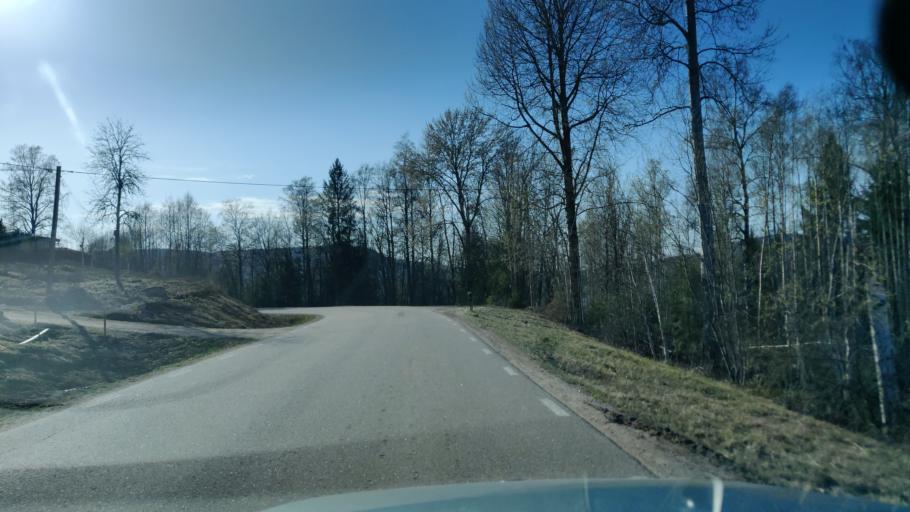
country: SE
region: Vaermland
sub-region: Munkfors Kommun
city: Munkfors
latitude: 59.9705
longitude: 13.4488
